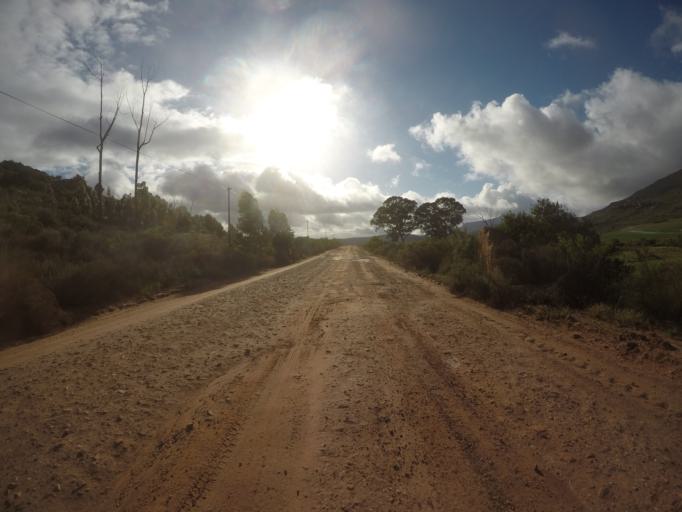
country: ZA
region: Western Cape
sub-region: West Coast District Municipality
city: Clanwilliam
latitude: -32.3435
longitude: 18.8199
